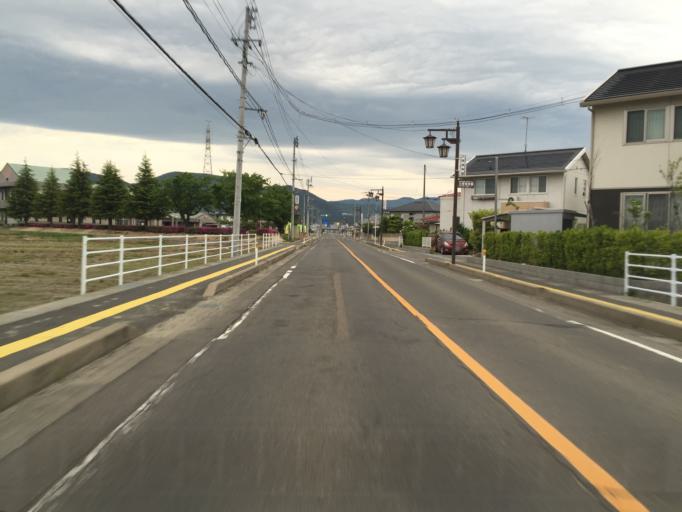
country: JP
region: Fukushima
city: Fukushima-shi
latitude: 37.7930
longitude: 140.4328
